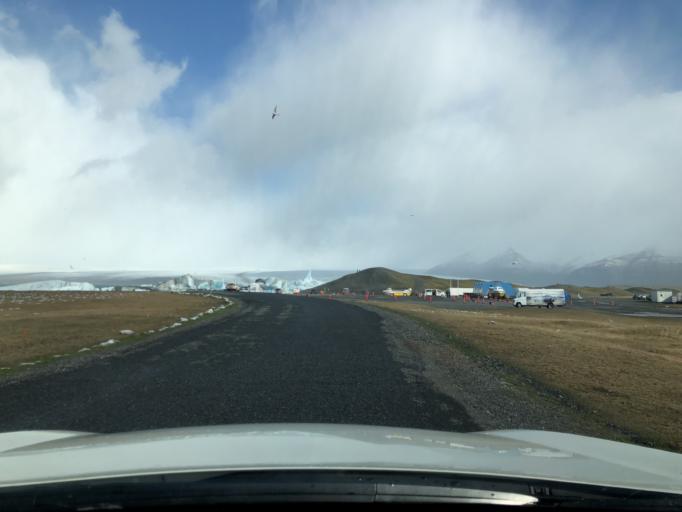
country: IS
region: East
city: Hoefn
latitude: 64.0470
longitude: -16.1783
